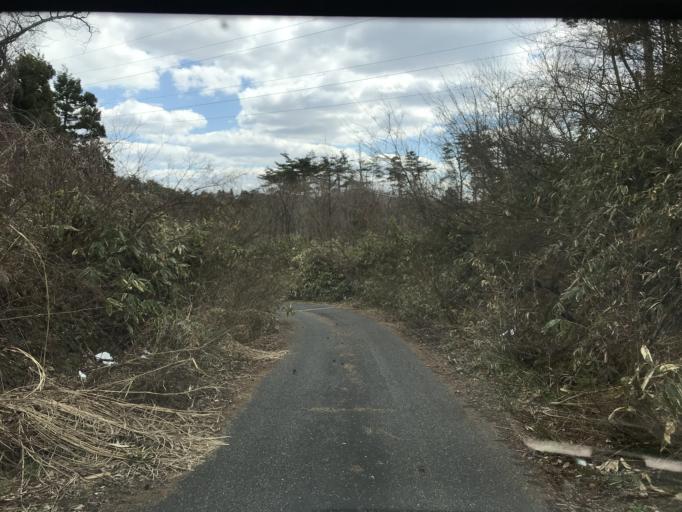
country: JP
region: Iwate
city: Ichinoseki
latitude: 38.9515
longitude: 141.0797
